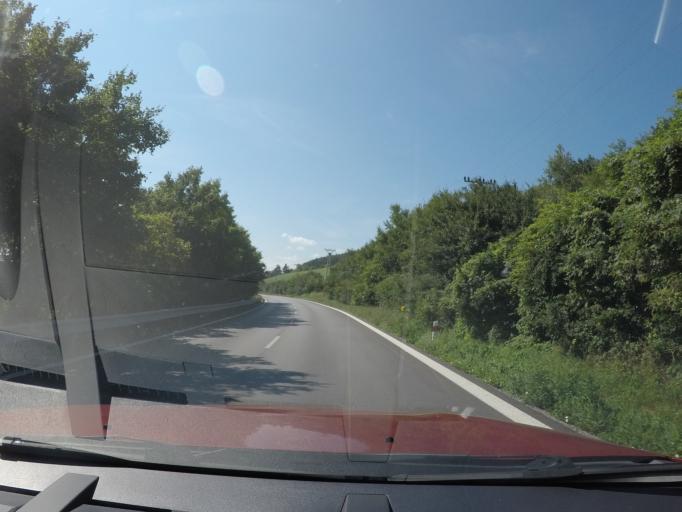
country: SK
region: Presovsky
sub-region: Okres Presov
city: Presov
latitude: 48.9160
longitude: 21.2396
